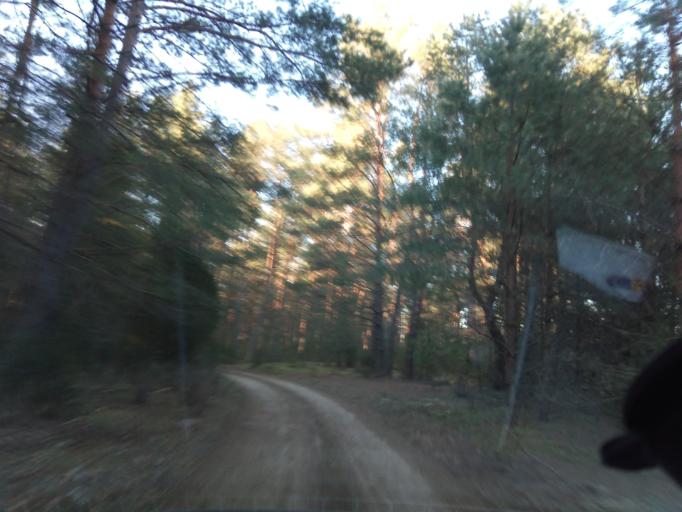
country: LT
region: Alytaus apskritis
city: Druskininkai
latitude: 53.9664
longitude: 23.9706
